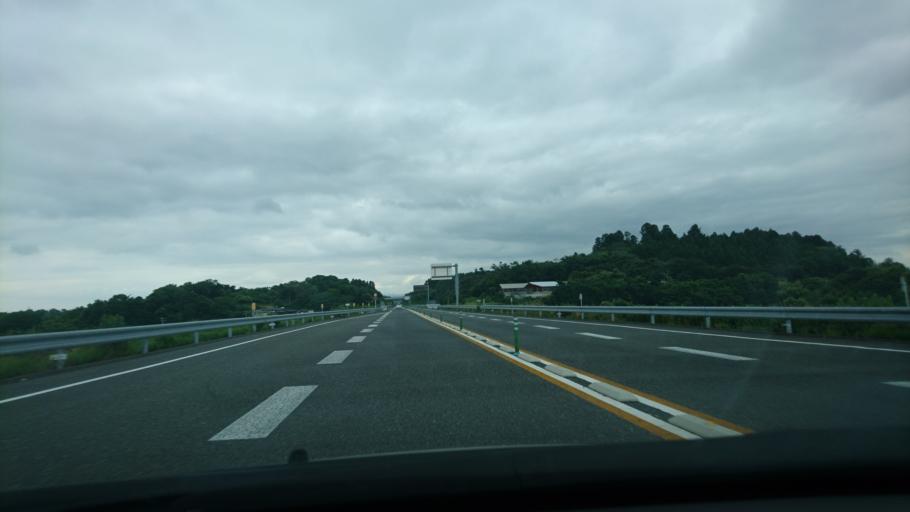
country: JP
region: Miyagi
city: Kogota
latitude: 38.7314
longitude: 141.0861
